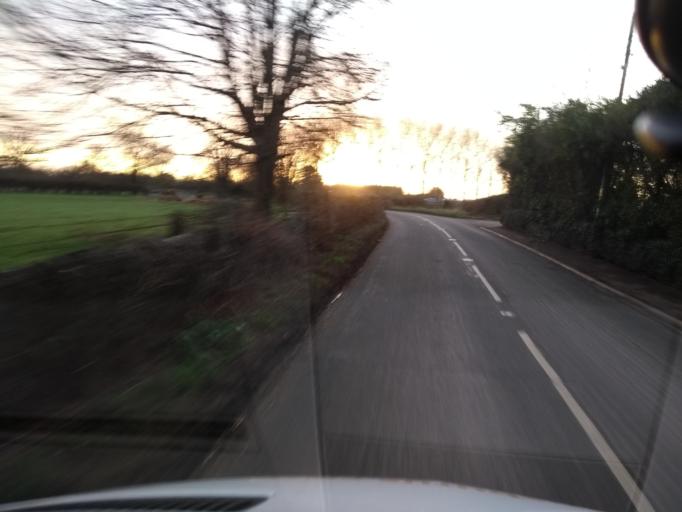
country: GB
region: England
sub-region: Somerset
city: Wedmore
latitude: 51.2245
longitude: -2.8465
